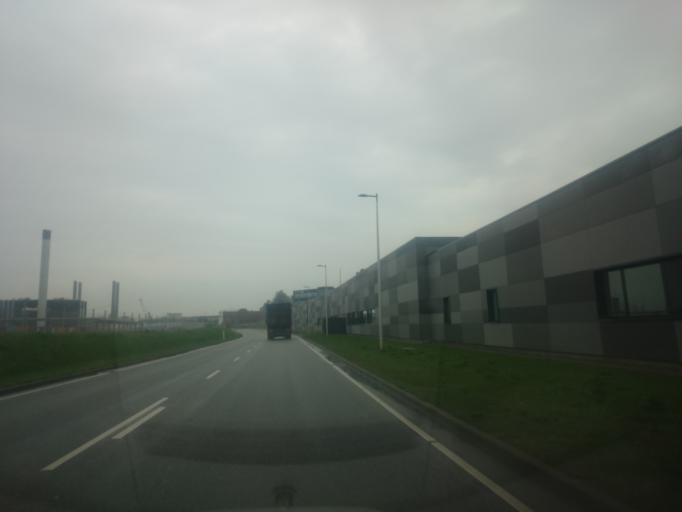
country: DK
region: South Denmark
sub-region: Esbjerg Kommune
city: Esbjerg
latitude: 55.4616
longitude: 8.4616
